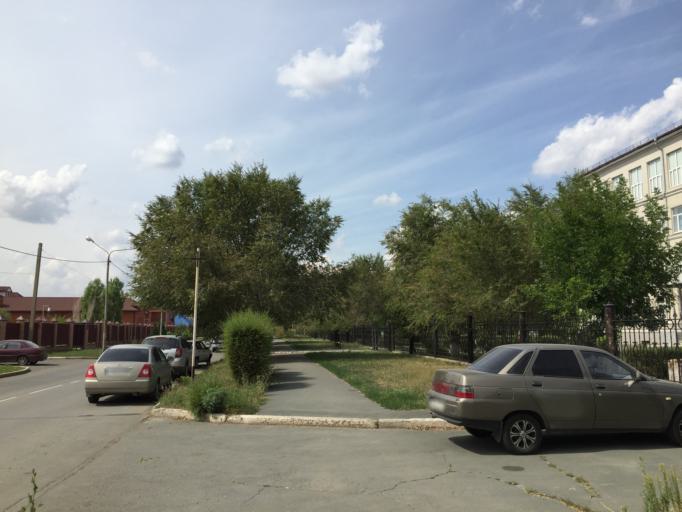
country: RU
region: Orenburg
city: Novotroitsk
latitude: 51.1940
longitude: 58.3106
